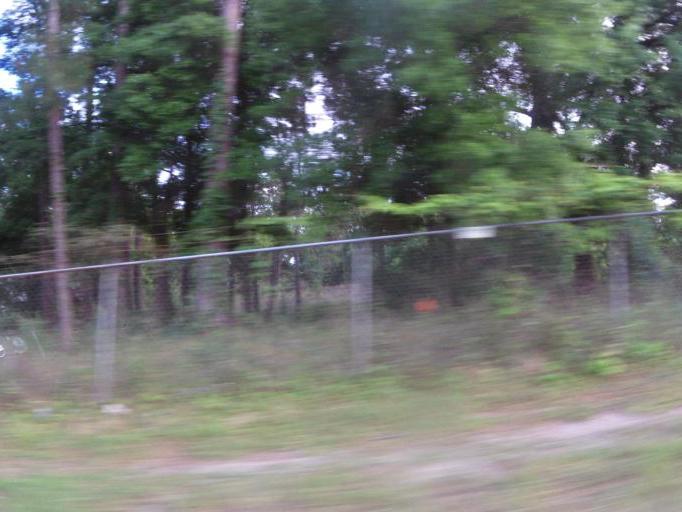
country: US
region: Florida
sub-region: Duval County
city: Jacksonville
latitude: 30.4481
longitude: -81.6376
